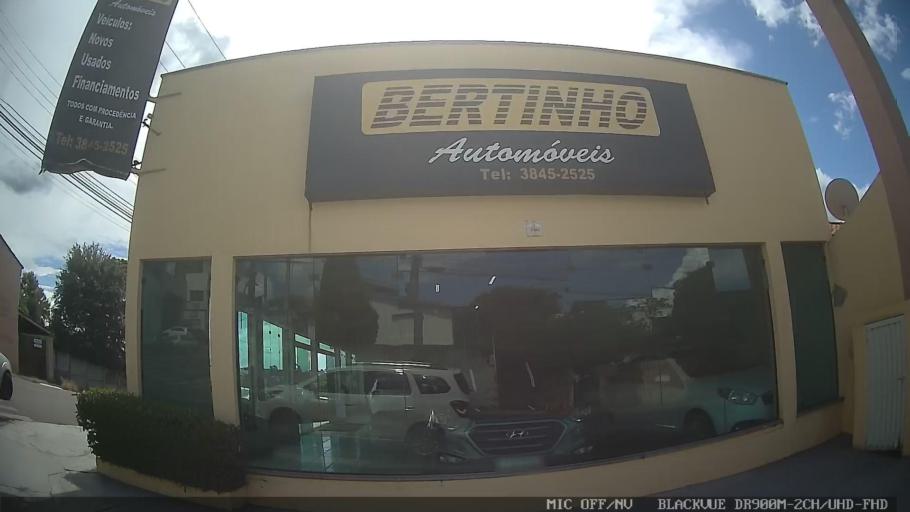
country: BR
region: Sao Paulo
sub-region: Conchas
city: Conchas
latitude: -23.0148
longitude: -48.0116
